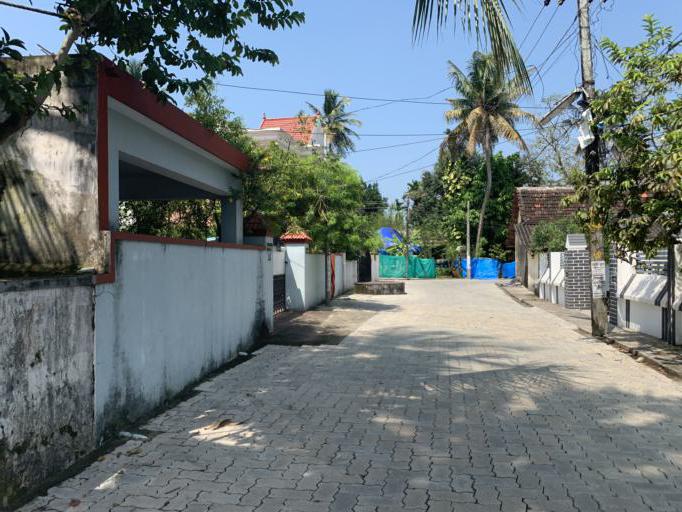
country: IN
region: Kerala
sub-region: Ernakulam
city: Cochin
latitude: 9.9774
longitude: 76.2406
